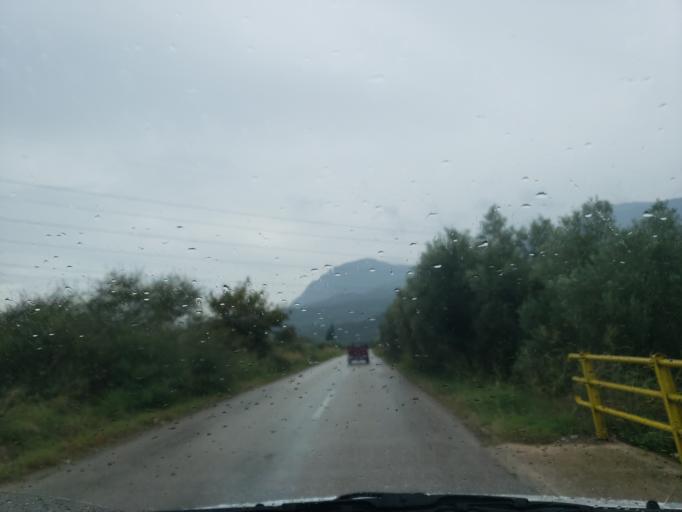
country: GR
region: Central Greece
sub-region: Nomos Fthiotidos
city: Anthili
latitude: 38.8017
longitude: 22.4615
